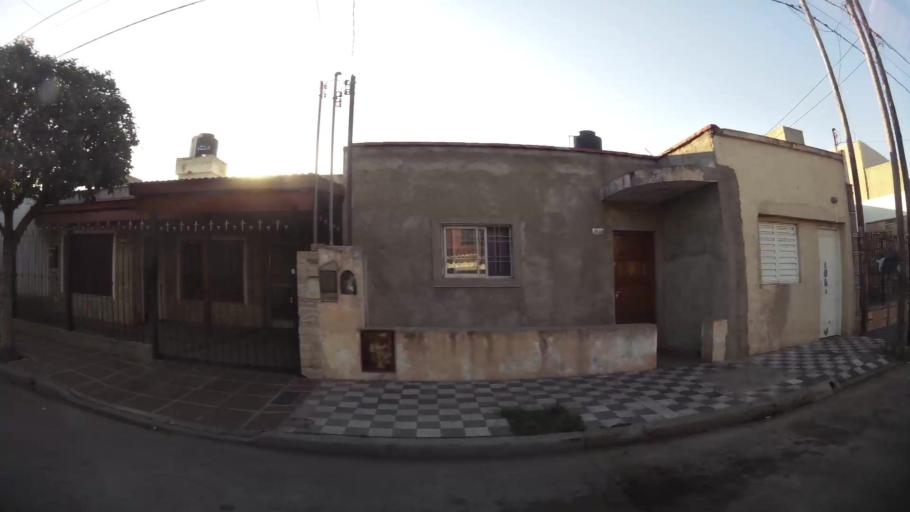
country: AR
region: Cordoba
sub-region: Departamento de Capital
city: Cordoba
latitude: -31.3754
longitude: -64.2080
